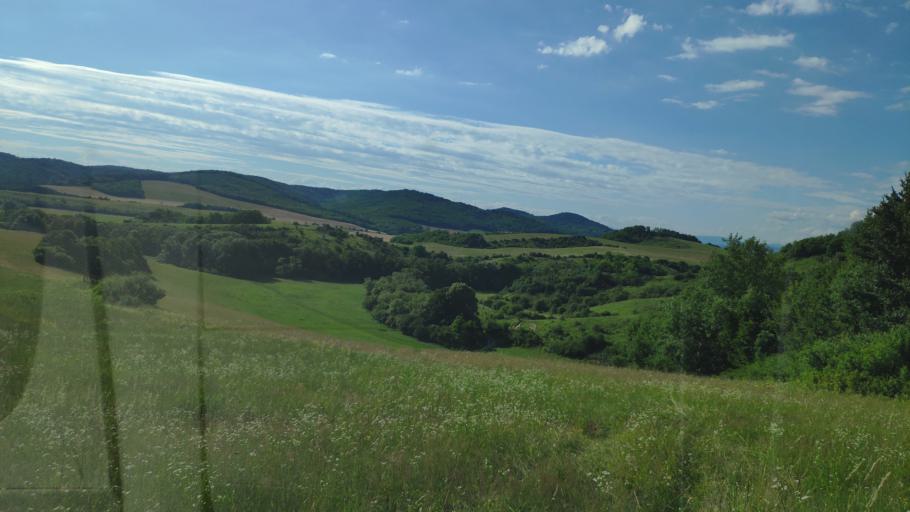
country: SK
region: Banskobystricky
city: Rimavska Sobota
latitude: 48.2461
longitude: 20.1104
